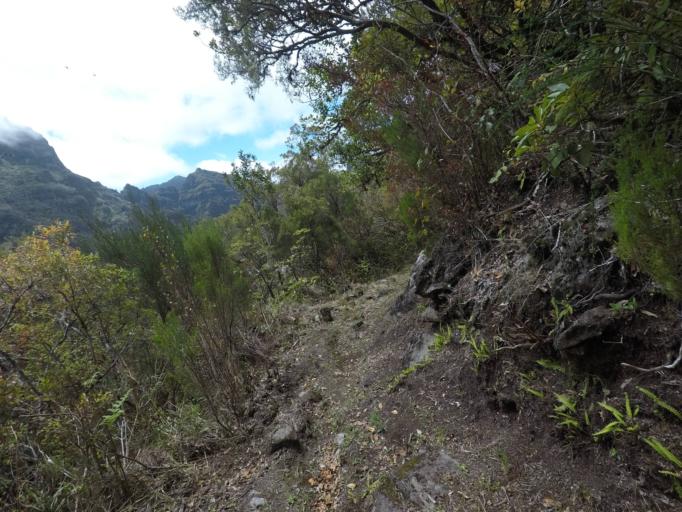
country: PT
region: Madeira
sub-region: Camara de Lobos
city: Curral das Freiras
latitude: 32.7649
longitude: -16.9750
